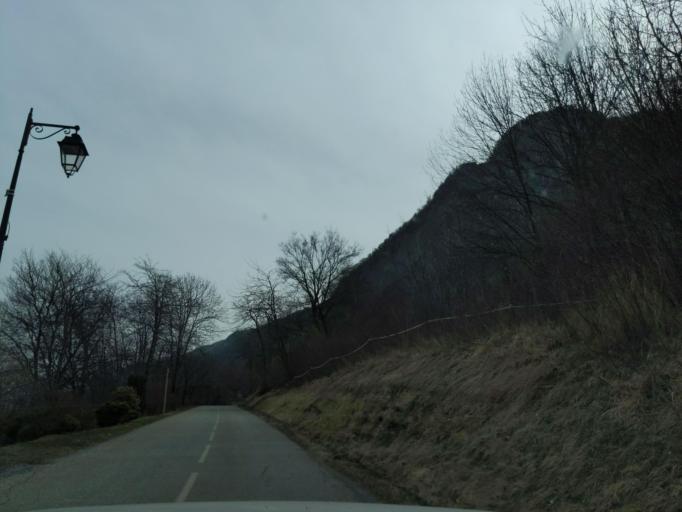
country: FR
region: Rhone-Alpes
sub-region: Departement de la Savoie
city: Villargondran
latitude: 45.2590
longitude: 6.3722
